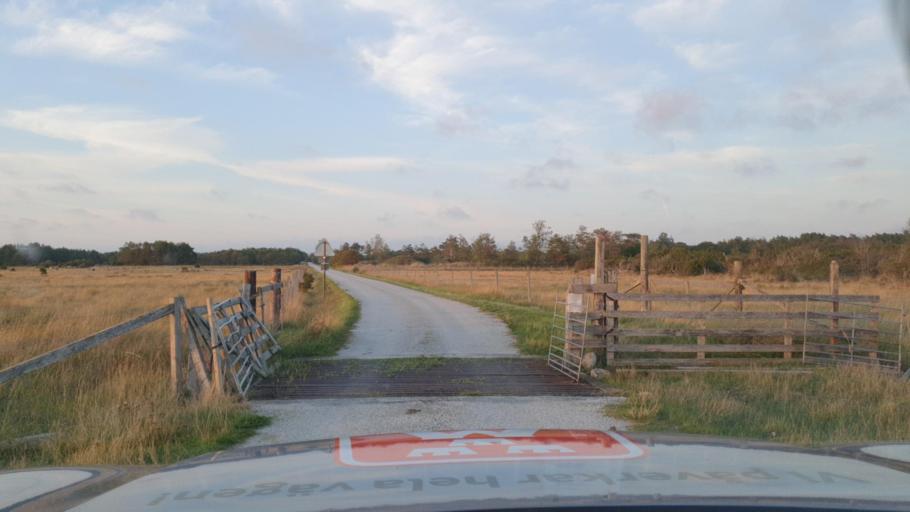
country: SE
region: Gotland
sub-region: Gotland
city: Klintehamn
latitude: 57.2571
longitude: 18.1141
